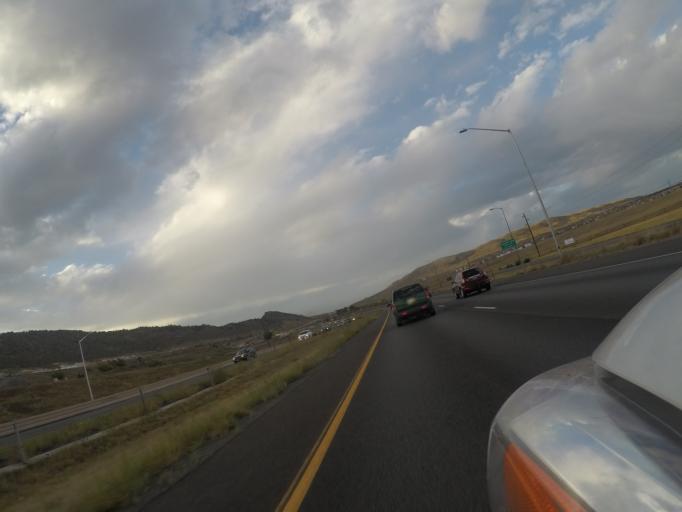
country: US
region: Colorado
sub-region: Jefferson County
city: Indian Hills
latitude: 39.6554
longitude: -105.1815
